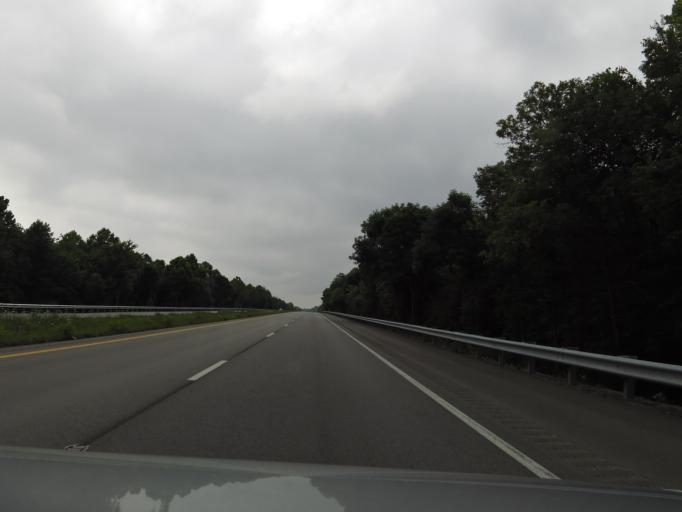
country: US
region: Kentucky
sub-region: Grayson County
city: Leitchfield
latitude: 37.4105
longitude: -86.4417
